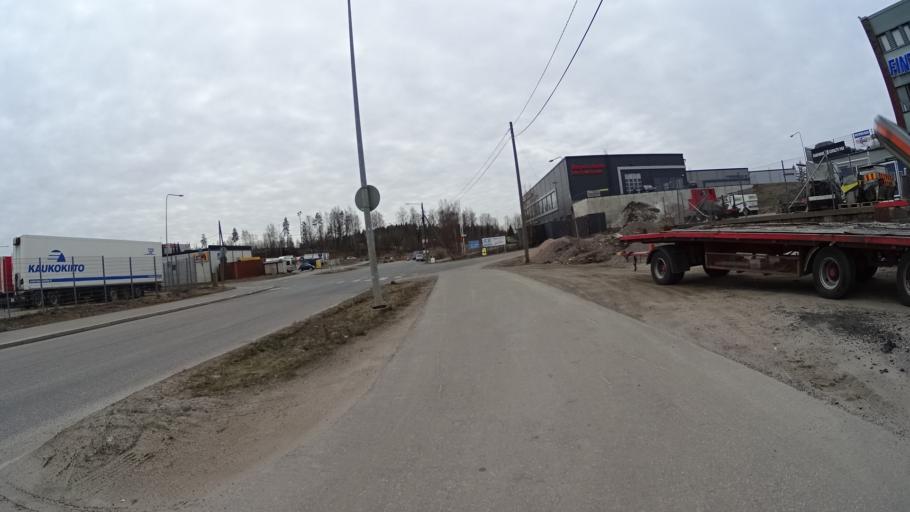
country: FI
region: Uusimaa
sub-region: Helsinki
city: Teekkarikylae
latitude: 60.3000
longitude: 24.9045
